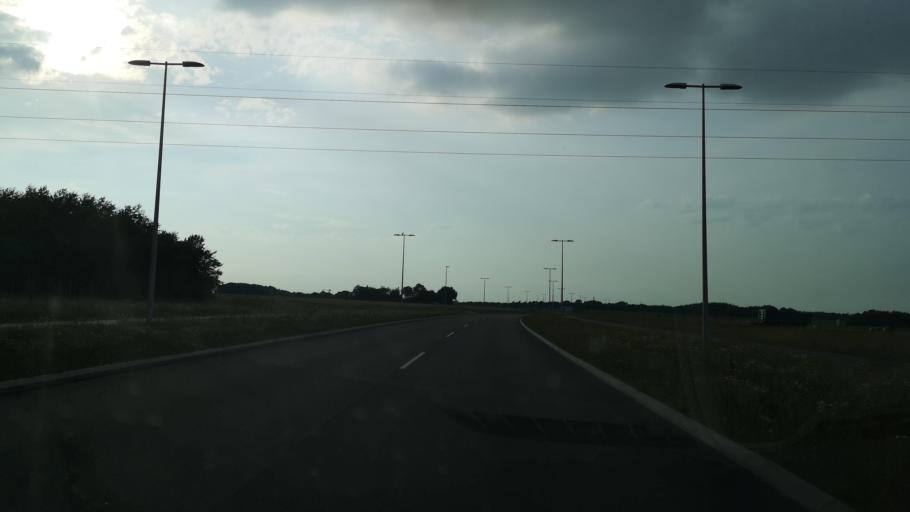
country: DK
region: Central Jutland
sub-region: Herning Kommune
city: Snejbjerg
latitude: 56.1210
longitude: 8.9198
